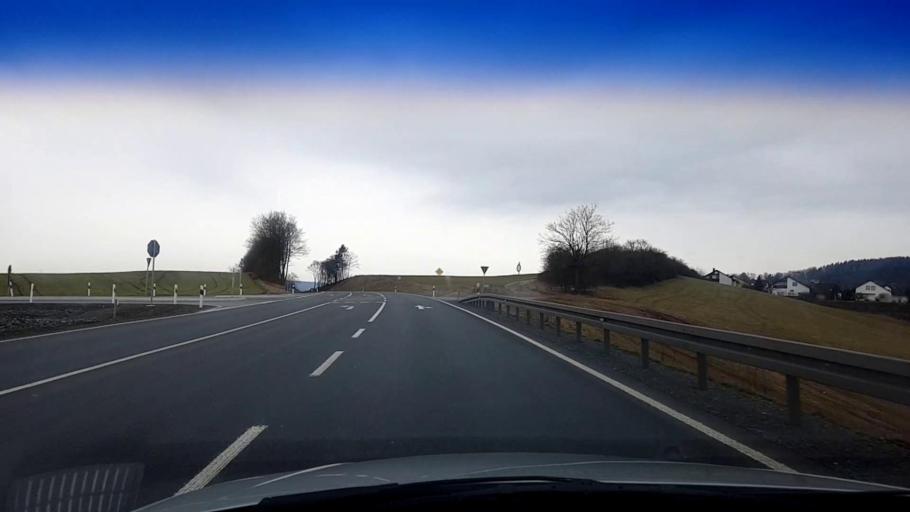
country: DE
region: Bavaria
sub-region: Upper Franconia
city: Kulmbach
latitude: 50.0835
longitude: 11.4626
